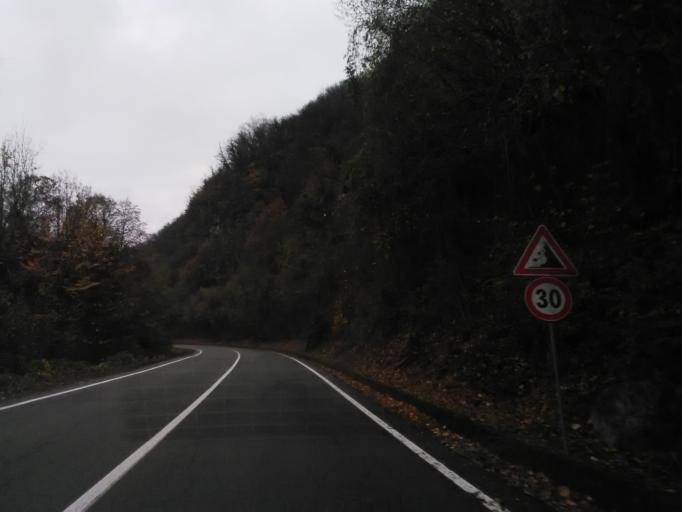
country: IT
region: Piedmont
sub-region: Provincia di Vercelli
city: Varallo
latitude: 45.7974
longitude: 8.2647
